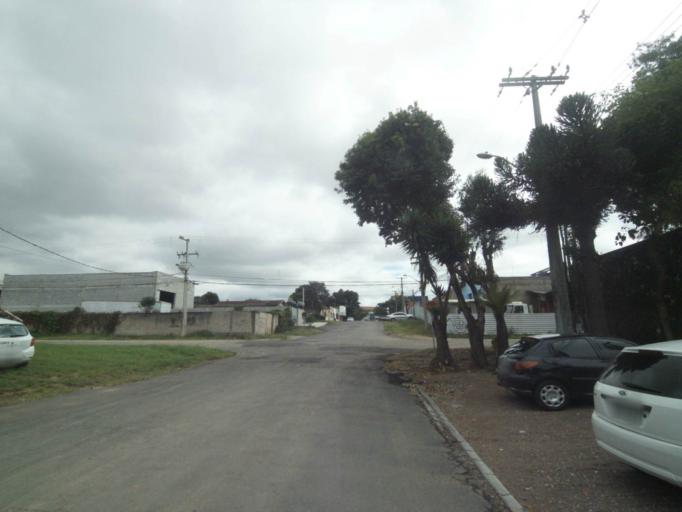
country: BR
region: Parana
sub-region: Curitiba
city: Curitiba
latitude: -25.4936
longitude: -49.2757
